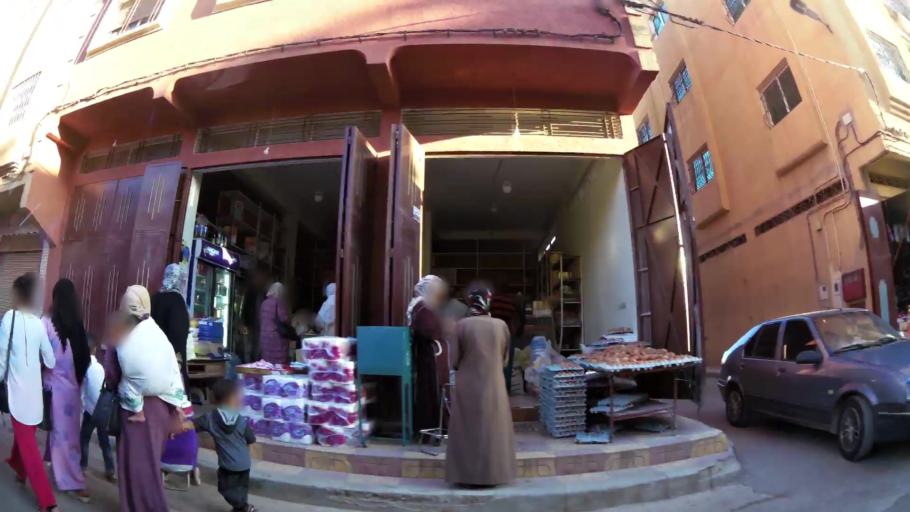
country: MA
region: Oriental
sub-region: Berkane-Taourirt
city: Berkane
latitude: 34.9217
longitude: -2.3159
